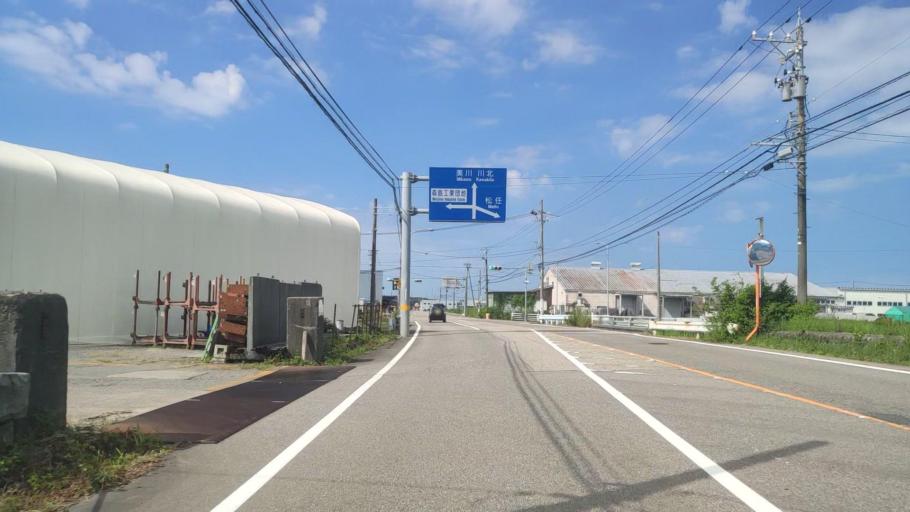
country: JP
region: Ishikawa
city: Tsurugi-asahimachi
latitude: 36.4683
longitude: 136.5938
